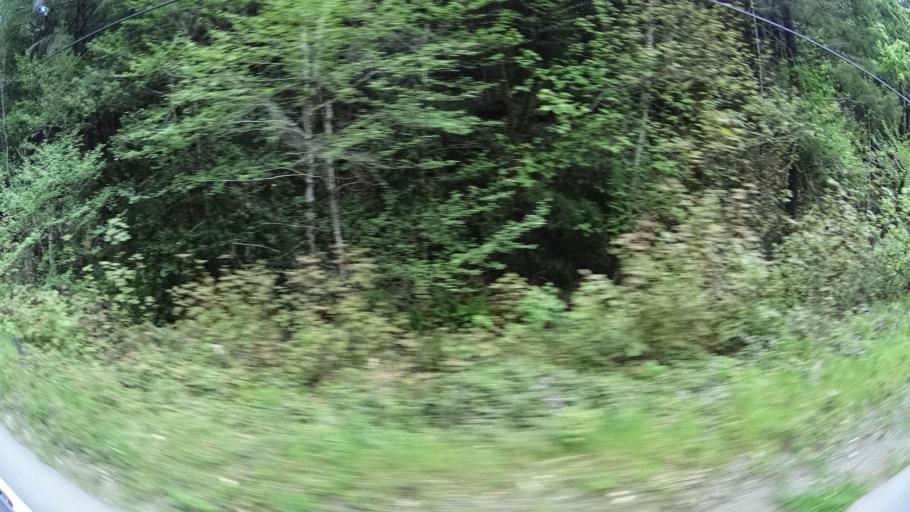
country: US
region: California
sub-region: Humboldt County
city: Redway
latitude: 40.0842
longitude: -123.9486
